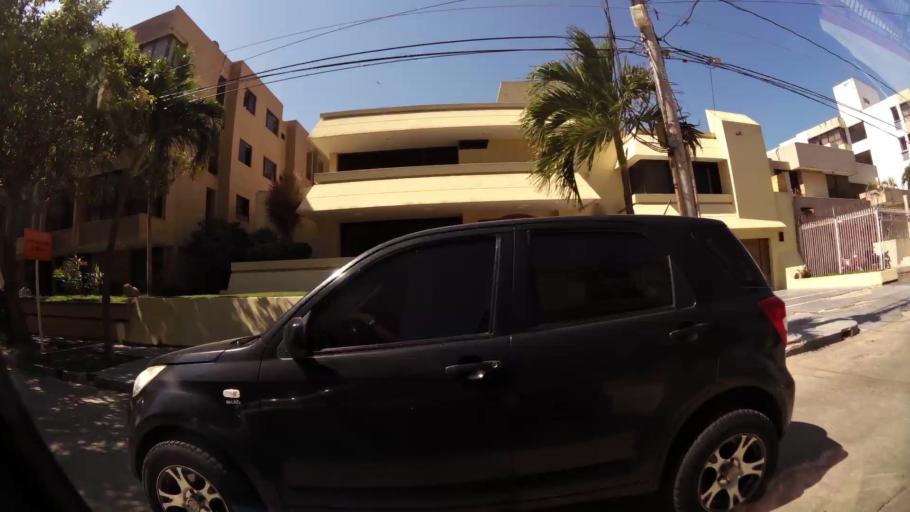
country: CO
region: Atlantico
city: Barranquilla
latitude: 11.0159
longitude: -74.8185
